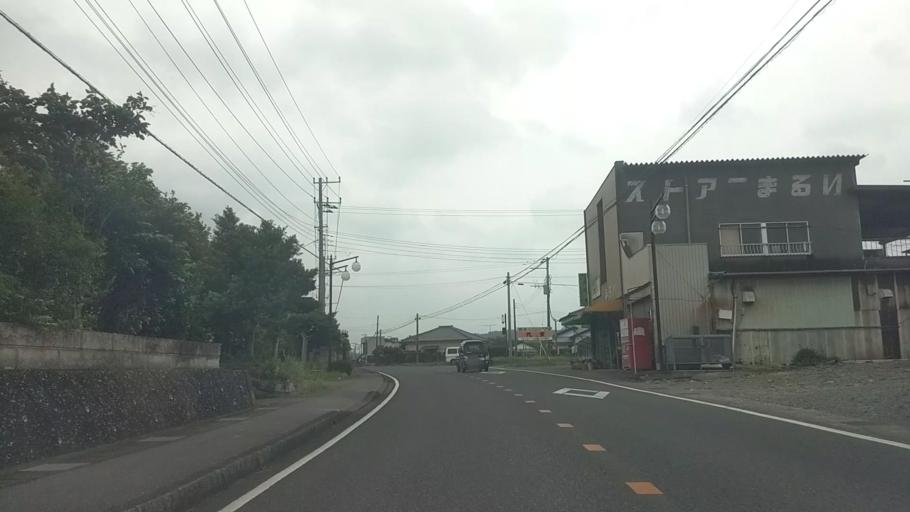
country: JP
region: Chiba
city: Kimitsu
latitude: 35.2169
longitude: 139.8968
